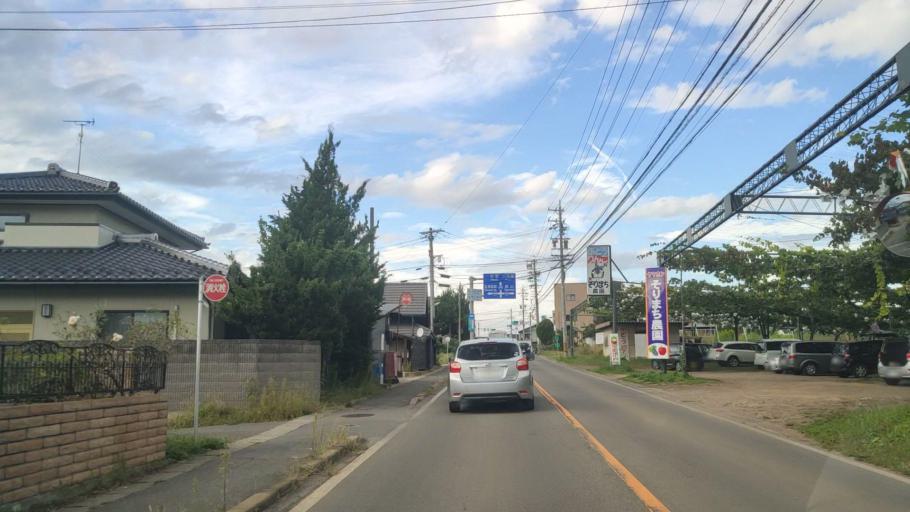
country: JP
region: Nagano
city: Suzaka
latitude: 36.6769
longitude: 138.3174
